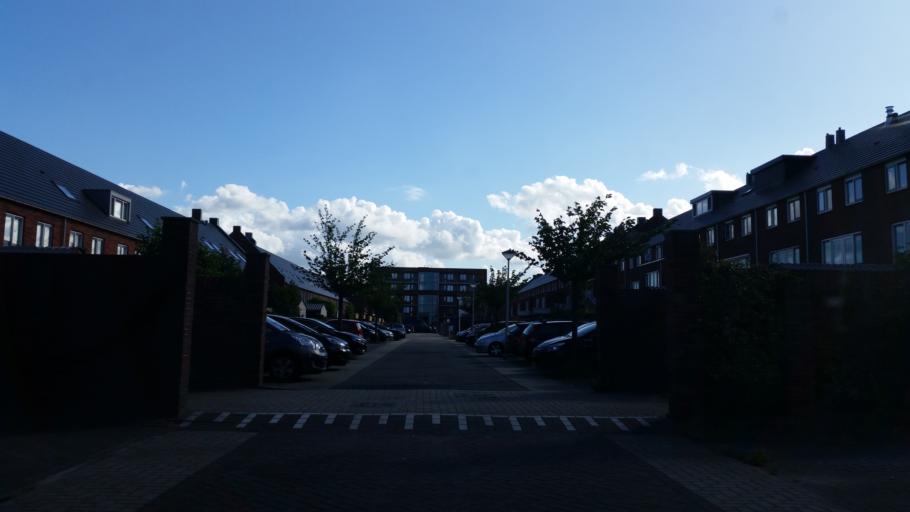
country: NL
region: South Holland
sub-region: Gemeente Lansingerland
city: Bergschenhoek
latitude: 51.9958
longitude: 4.4926
